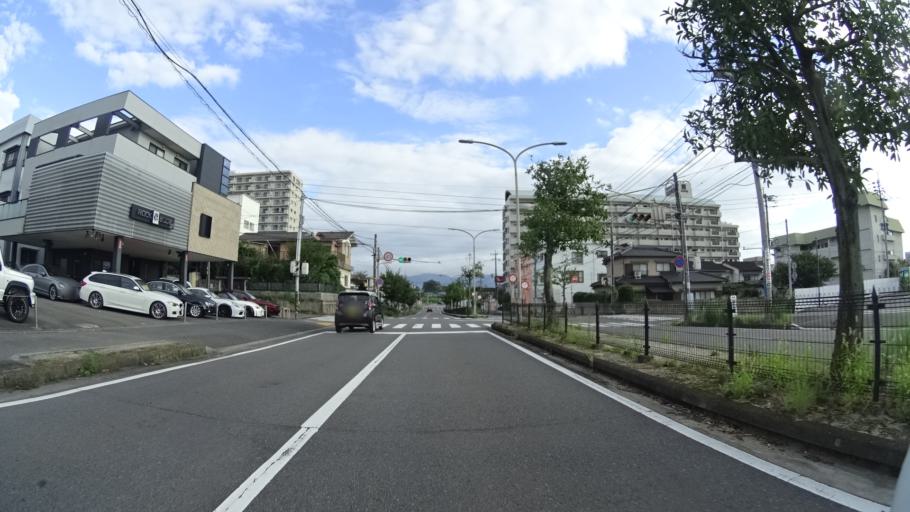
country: JP
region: Oita
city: Beppu
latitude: 33.3035
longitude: 131.4948
